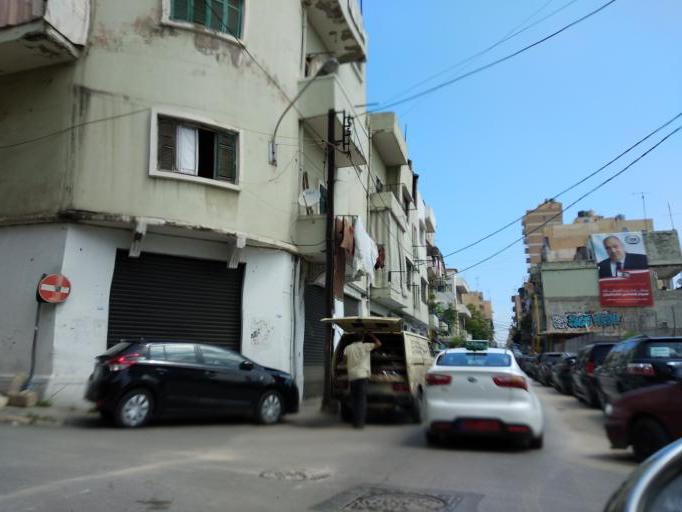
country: LB
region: Mont-Liban
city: Jdaidet el Matn
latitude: 33.8919
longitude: 35.5330
